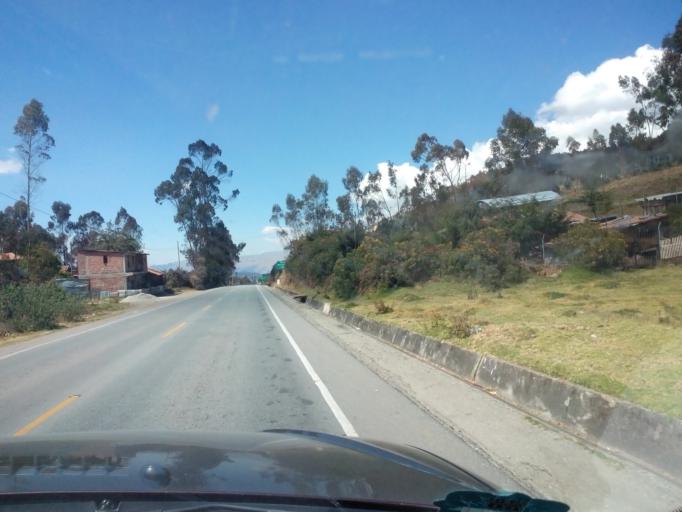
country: PE
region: Cusco
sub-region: Provincia de Anta
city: Ancahuasi
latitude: -13.4399
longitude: -72.3582
